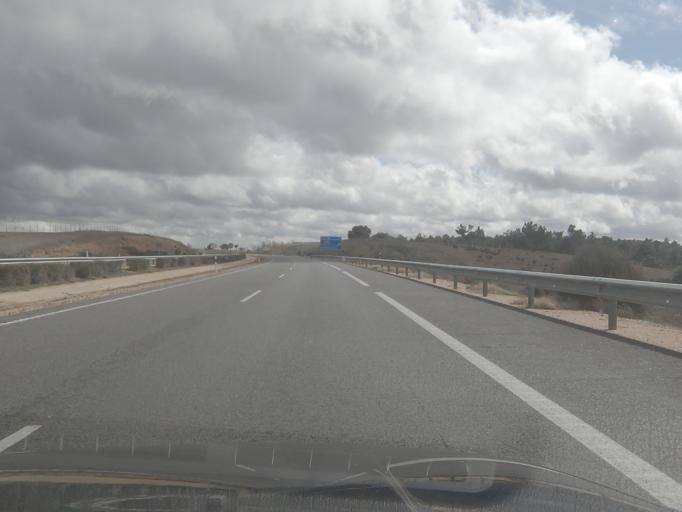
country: ES
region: Castille and Leon
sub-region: Provincia de Zamora
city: Cuelgamures
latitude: 41.2740
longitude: -5.7059
